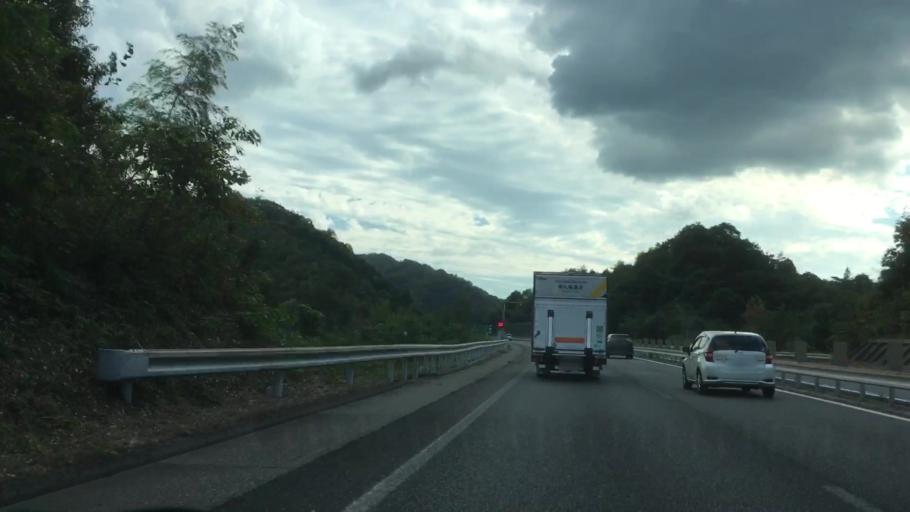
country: JP
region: Yamaguchi
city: Iwakuni
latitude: 34.1289
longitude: 132.1117
